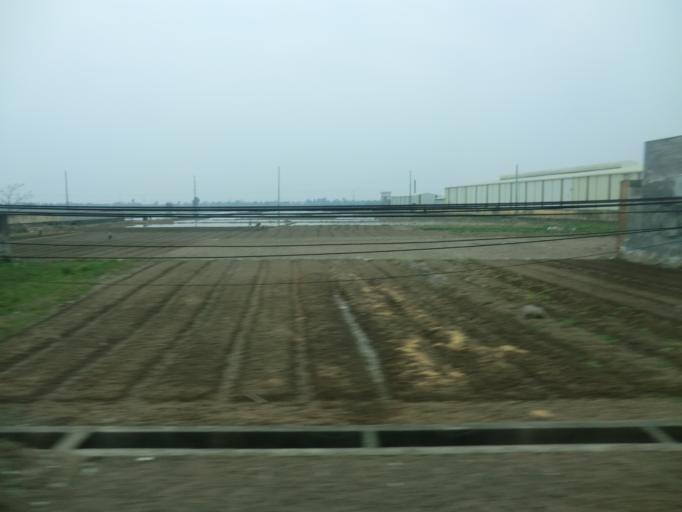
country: VN
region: Nam Dinh
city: Thi Tran Goi
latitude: 20.3611
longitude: 106.1258
